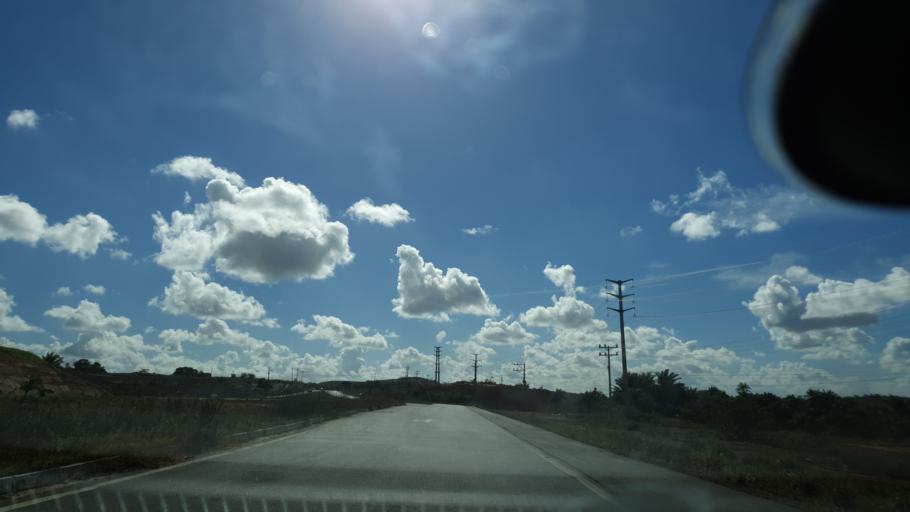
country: BR
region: Bahia
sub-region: Camacari
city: Camacari
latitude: -12.6831
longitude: -38.2470
